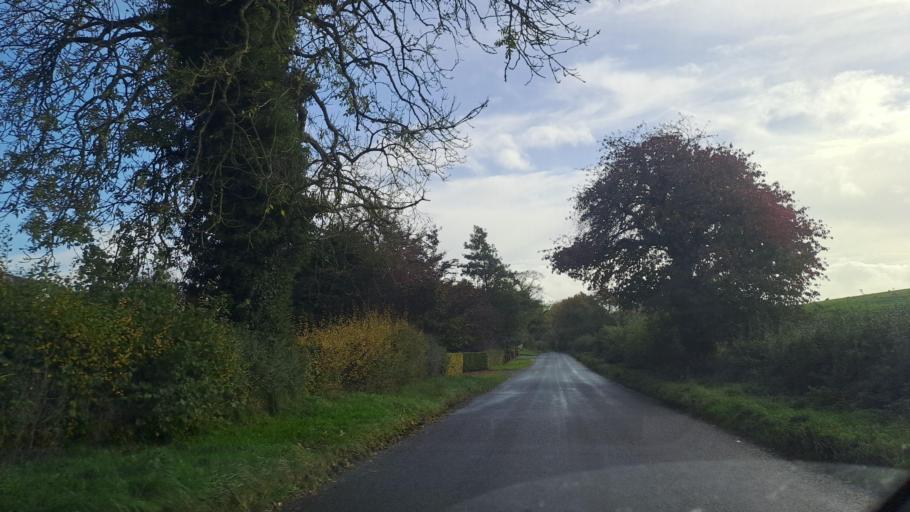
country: IE
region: Leinster
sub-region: Lu
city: Ardee
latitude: 53.8665
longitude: -6.6607
